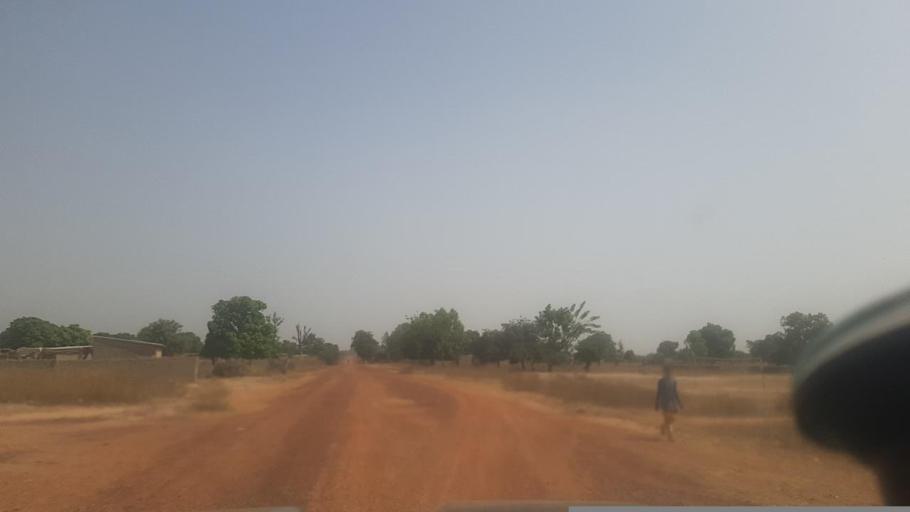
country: ML
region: Segou
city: Segou
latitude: 12.9325
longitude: -6.2880
